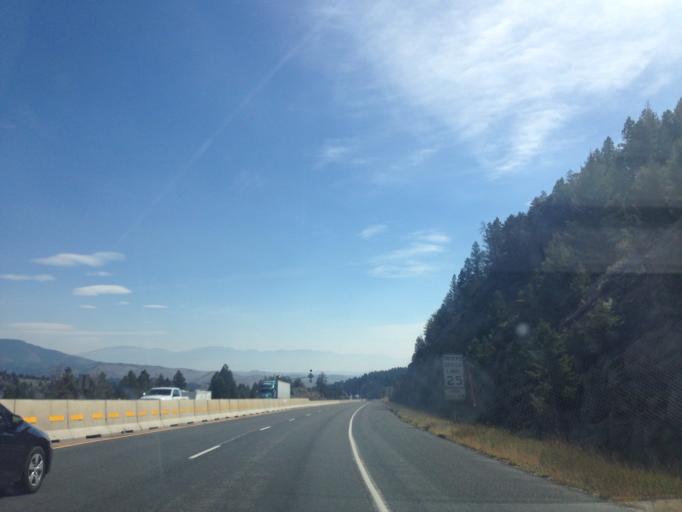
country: US
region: Montana
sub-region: Jefferson County
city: Whitehall
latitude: 45.9099
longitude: -112.3192
